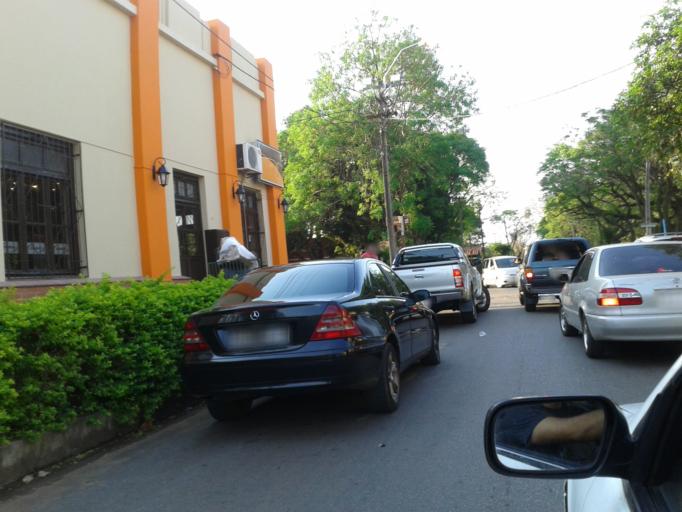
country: PY
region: Guaira
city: Villarrica
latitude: -25.7721
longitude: -56.4471
